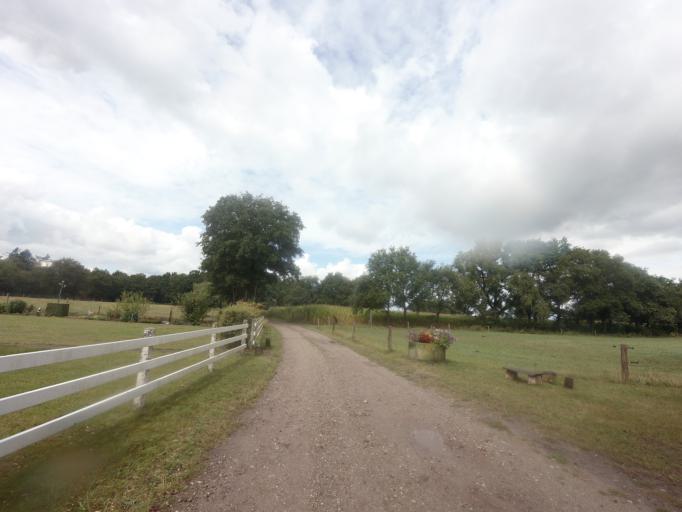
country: NL
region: Overijssel
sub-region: Gemeente Staphorst
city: Staphorst
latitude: 52.6167
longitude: 6.3190
